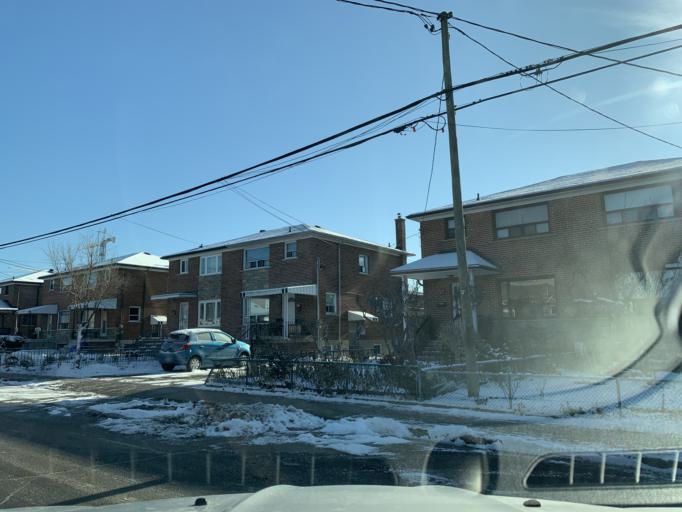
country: CA
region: Ontario
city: Toronto
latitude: 43.6711
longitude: -79.4827
